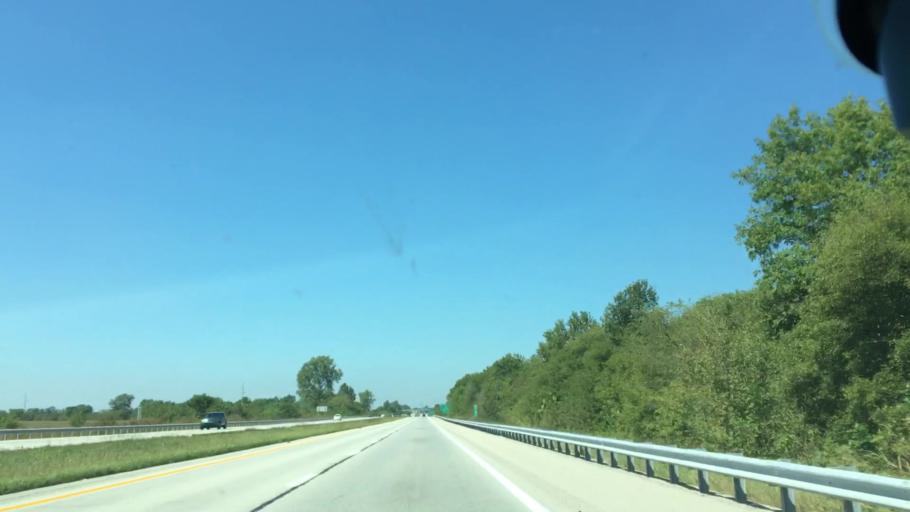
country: US
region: Kentucky
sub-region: Henderson County
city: Henderson
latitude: 37.7830
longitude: -87.5465
